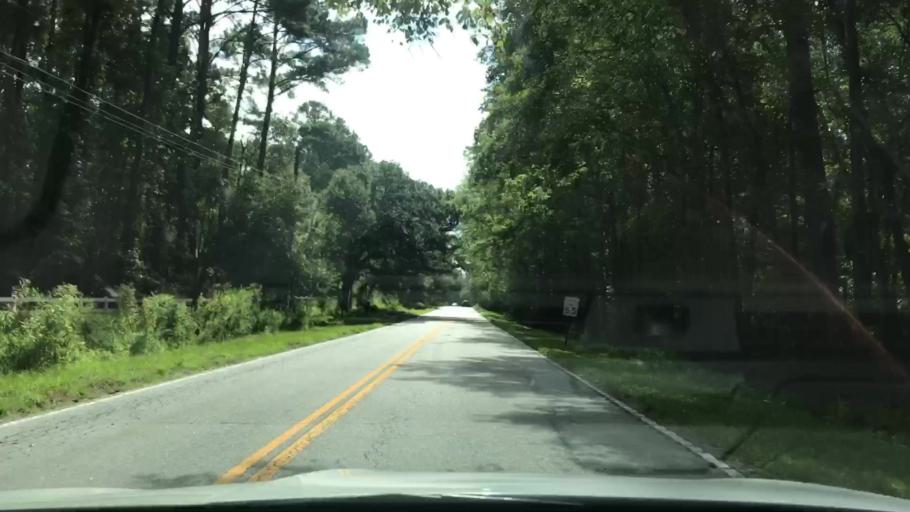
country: US
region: South Carolina
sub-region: Dorchester County
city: Centerville
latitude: 32.9462
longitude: -80.1999
